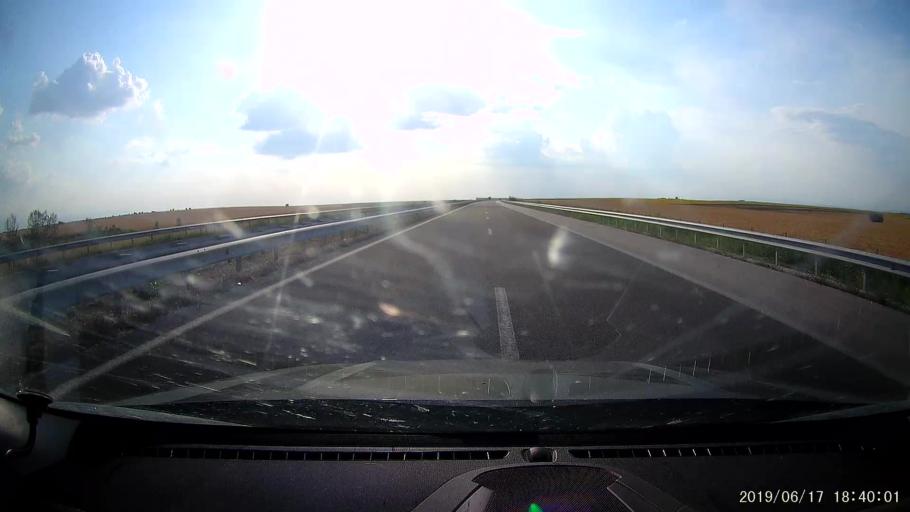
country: BG
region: Stara Zagora
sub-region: Obshtina Chirpan
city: Chirpan
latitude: 42.1508
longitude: 25.2900
